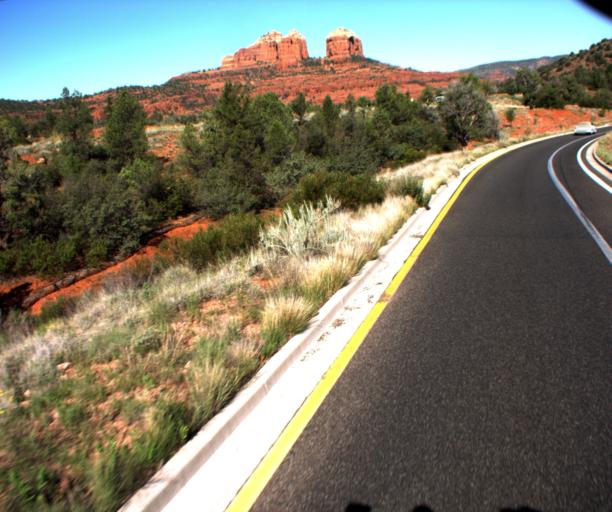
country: US
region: Arizona
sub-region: Yavapai County
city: Village of Oak Creek (Big Park)
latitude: 34.8180
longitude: -111.7709
